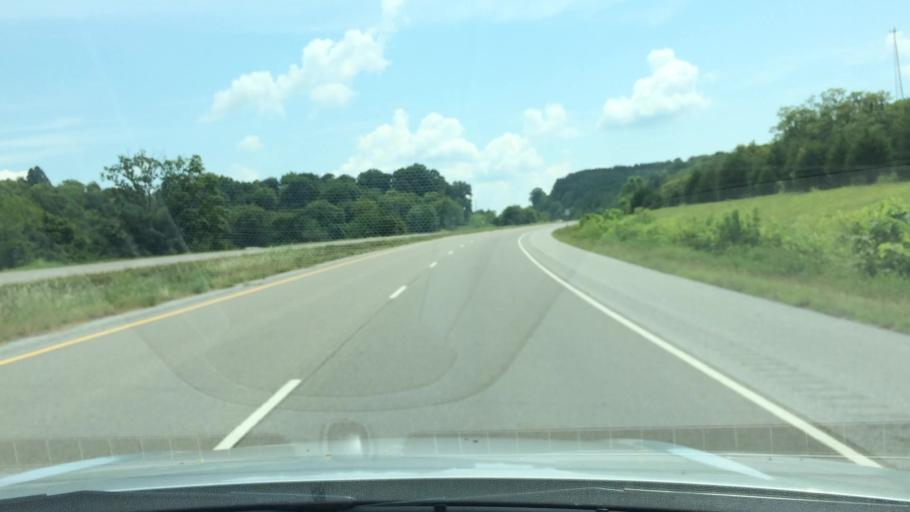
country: US
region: Tennessee
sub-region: Giles County
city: Pulaski
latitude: 35.1753
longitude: -86.9977
